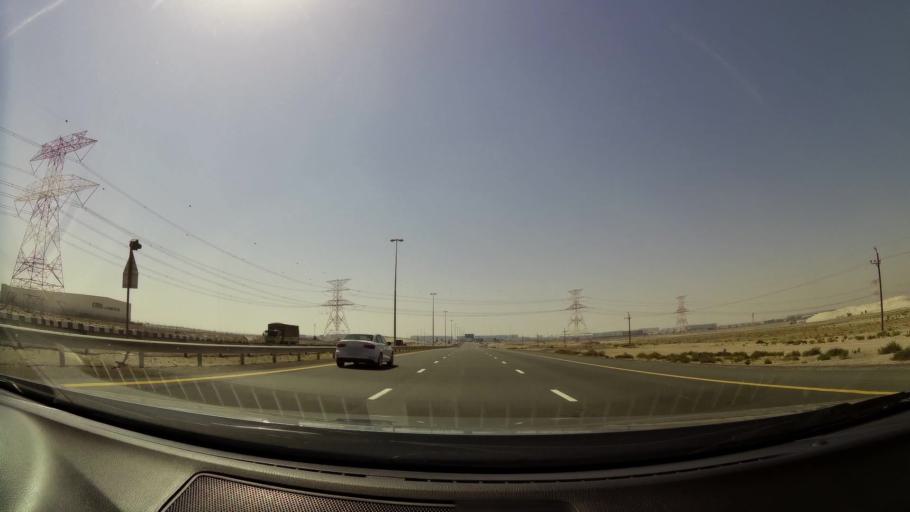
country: AE
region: Dubai
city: Dubai
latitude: 24.9245
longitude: 55.0960
